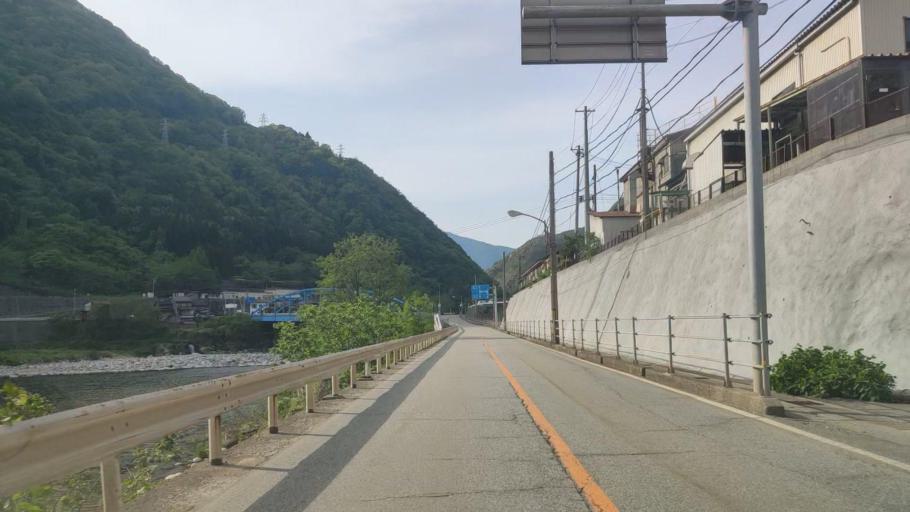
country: JP
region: Gifu
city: Takayama
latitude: 36.3383
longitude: 137.2975
